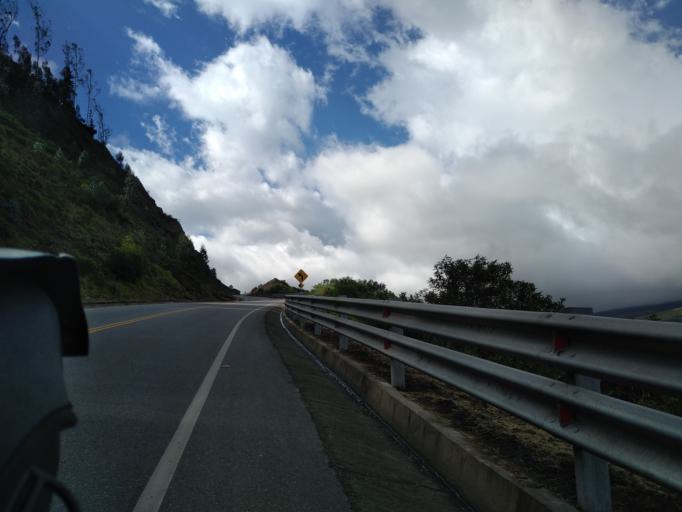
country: EC
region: Tungurahua
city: Banos
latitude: -1.4914
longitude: -78.5176
